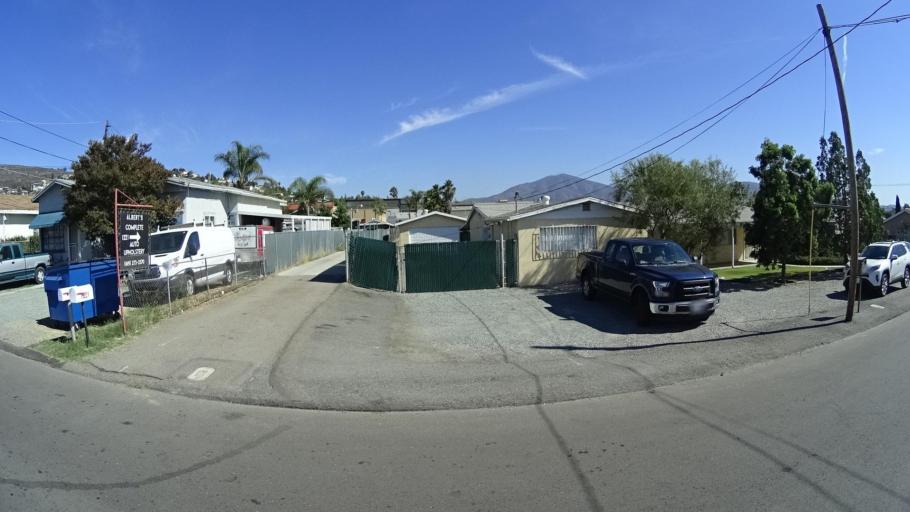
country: US
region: California
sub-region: San Diego County
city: La Presa
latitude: 32.7158
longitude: -117.0015
